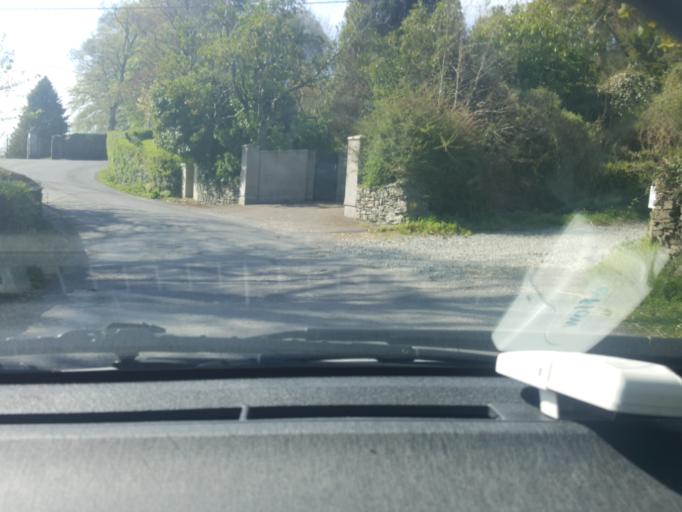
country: IE
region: Munster
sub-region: County Cork
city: Bandon
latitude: 51.7667
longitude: -8.6638
